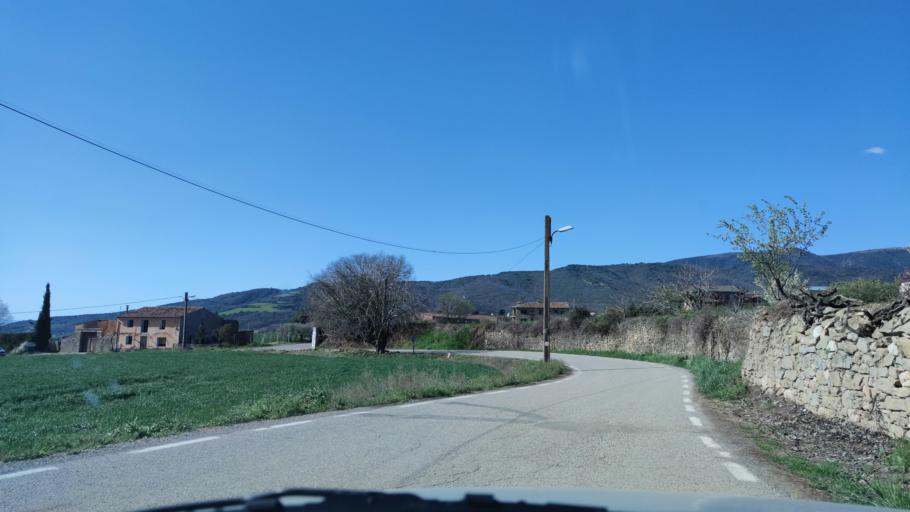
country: ES
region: Catalonia
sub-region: Provincia de Lleida
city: Artesa de Segre
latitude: 41.9934
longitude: 1.0232
